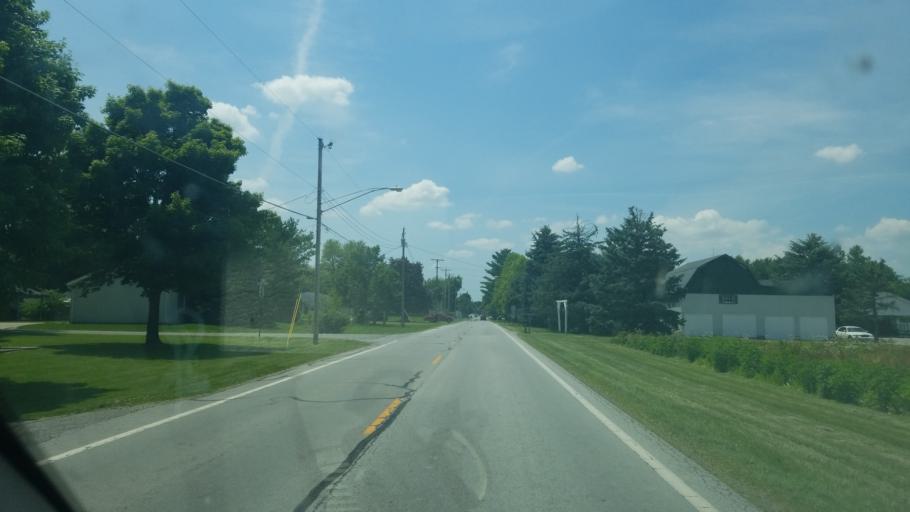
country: US
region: Ohio
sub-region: Hardin County
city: Ada
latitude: 40.7767
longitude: -83.8173
